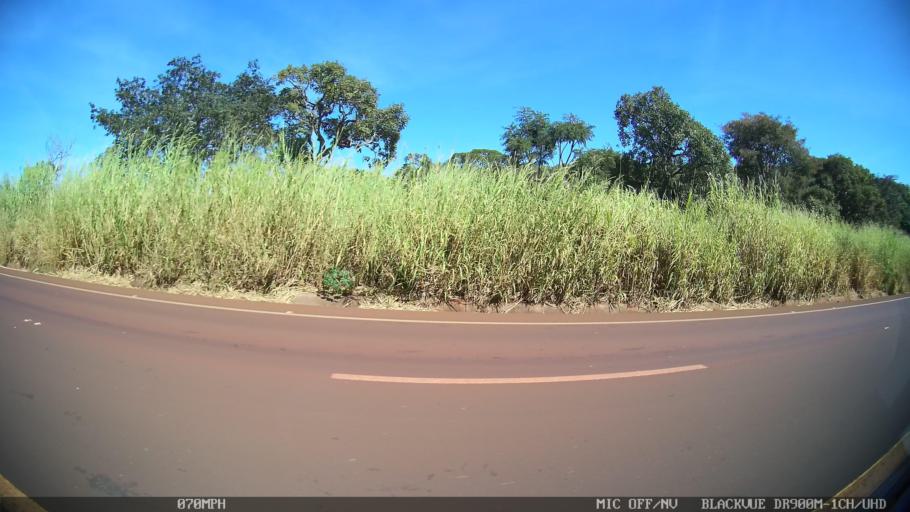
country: BR
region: Sao Paulo
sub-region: Nuporanga
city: Nuporanga
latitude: -20.5506
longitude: -47.6480
